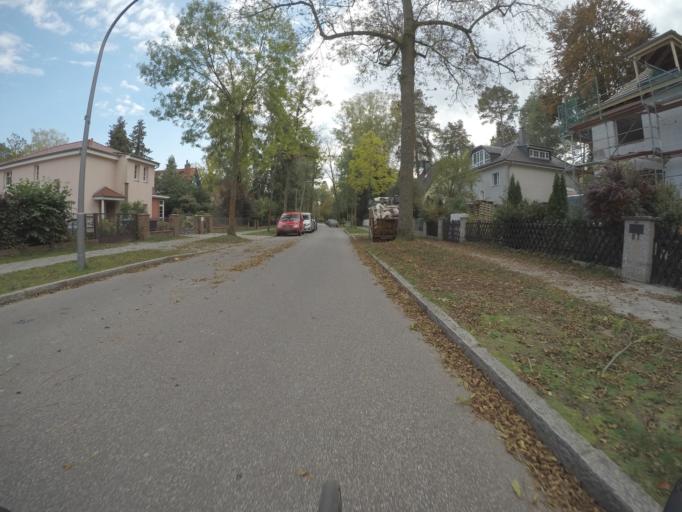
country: DE
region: Berlin
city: Frohnau
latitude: 52.6378
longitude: 13.2774
